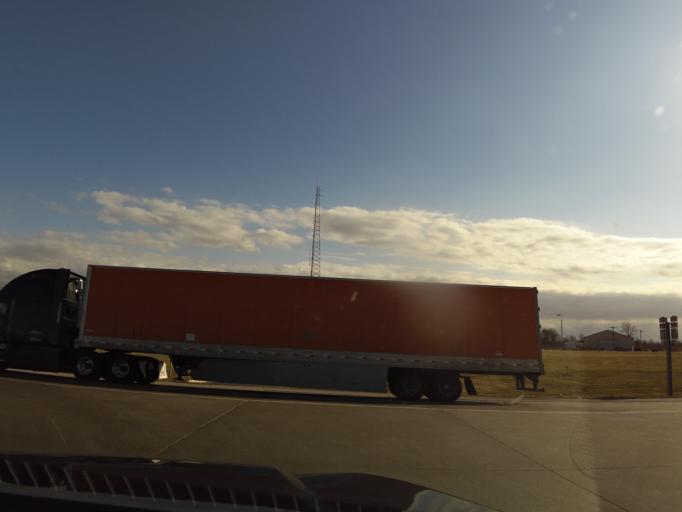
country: US
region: Missouri
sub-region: Ralls County
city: New London
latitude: 39.5730
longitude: -91.4036
